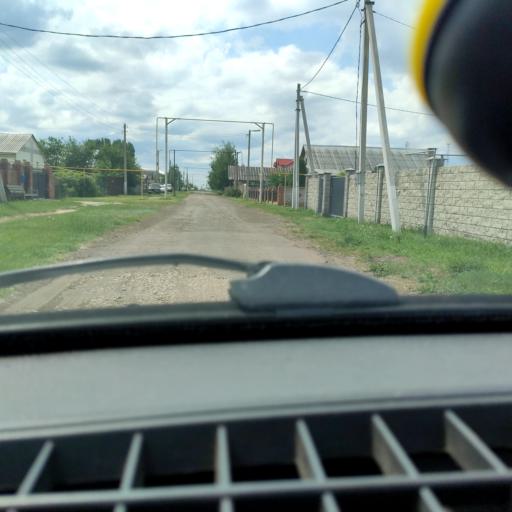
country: RU
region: Samara
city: Povolzhskiy
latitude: 53.6476
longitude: 49.6913
